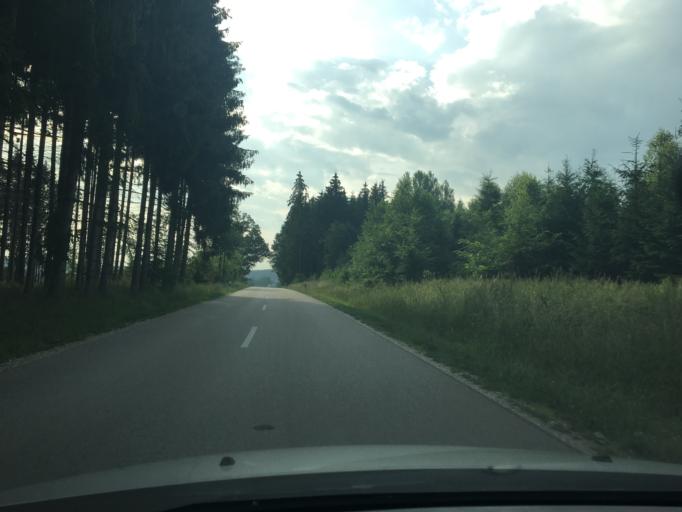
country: DE
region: Bavaria
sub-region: Lower Bavaria
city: Bodenkirchen
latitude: 48.3874
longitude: 12.3705
